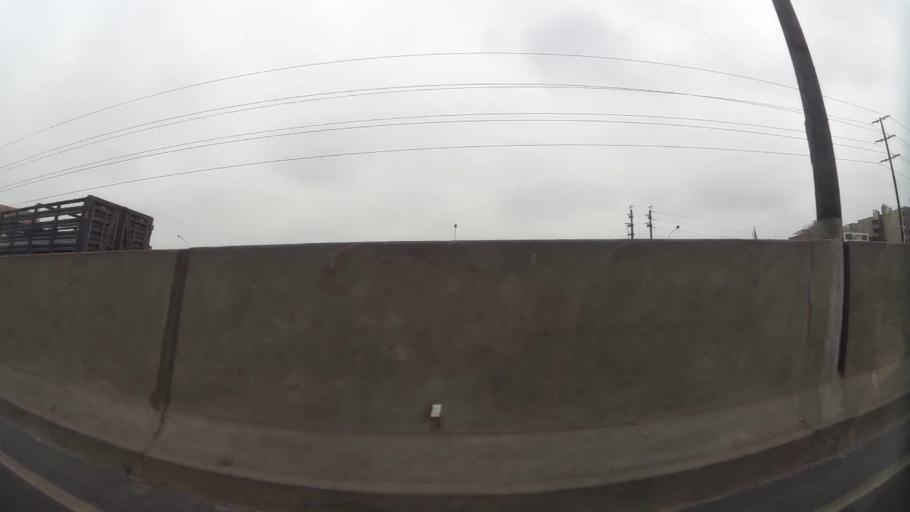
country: PE
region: Lima
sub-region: Lima
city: Independencia
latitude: -11.9504
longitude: -77.0703
